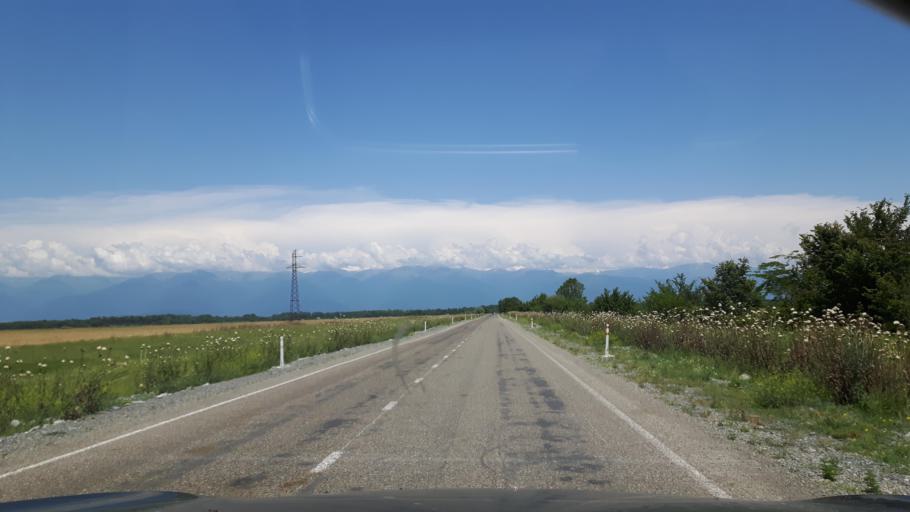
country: GE
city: Tsnori
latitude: 41.6506
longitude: 46.0546
